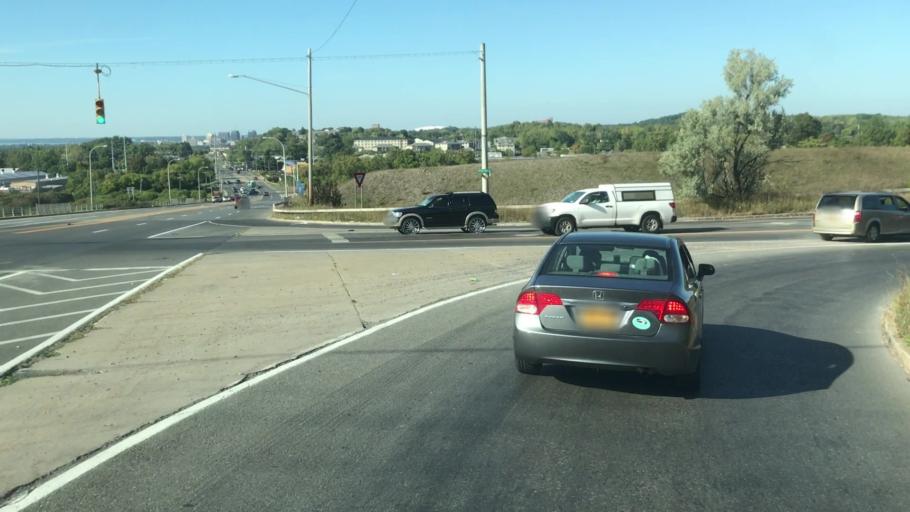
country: US
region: New York
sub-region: Onondaga County
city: Nedrow
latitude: 43.0057
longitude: -76.1312
